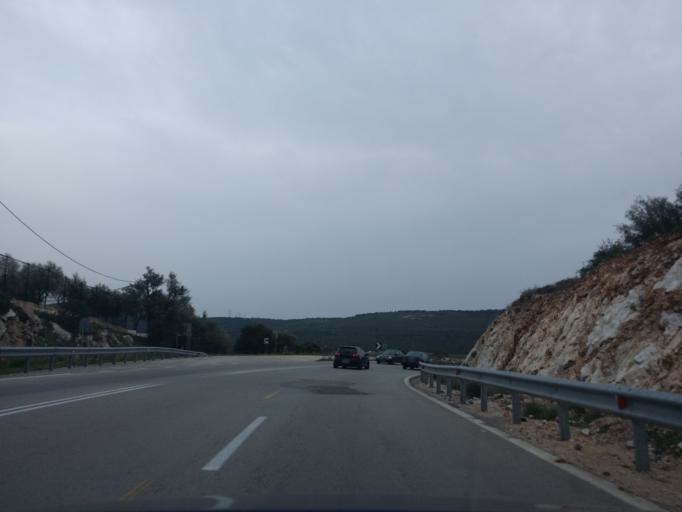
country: GR
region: Attica
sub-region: Nomarchia Dytikis Attikis
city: Vilia
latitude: 38.1565
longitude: 23.4310
